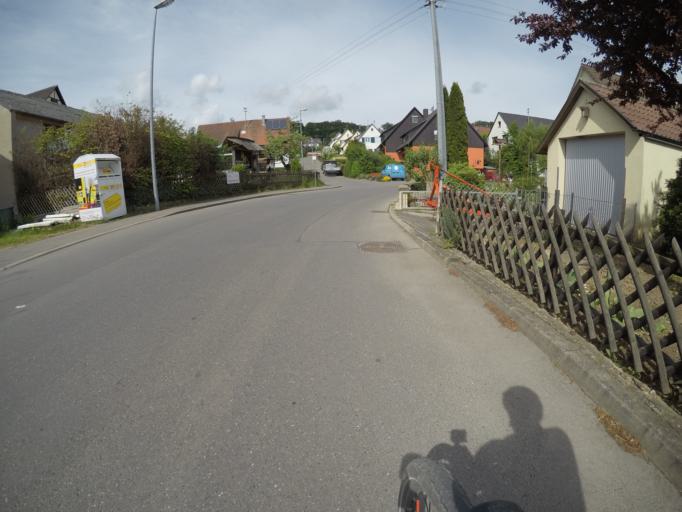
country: DE
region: Baden-Wuerttemberg
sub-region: Tuebingen Region
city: Tuebingen
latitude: 48.5417
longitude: 9.0097
